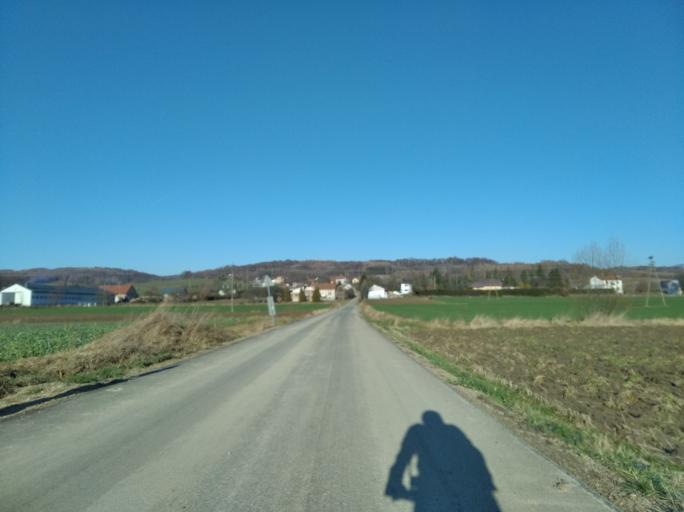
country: PL
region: Subcarpathian Voivodeship
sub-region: Powiat strzyzowski
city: Wisniowa
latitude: 49.8710
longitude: 21.6954
